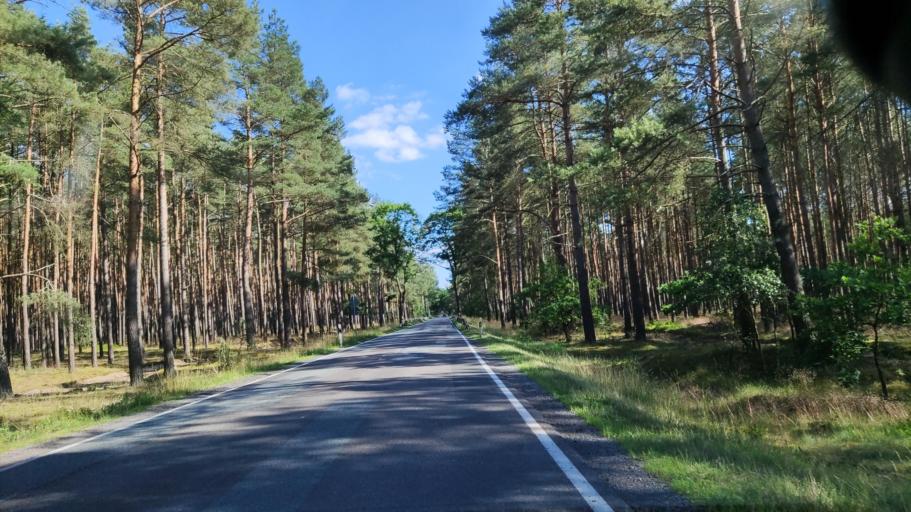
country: DE
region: Lower Saxony
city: Damnatz
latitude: 53.1930
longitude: 11.2077
